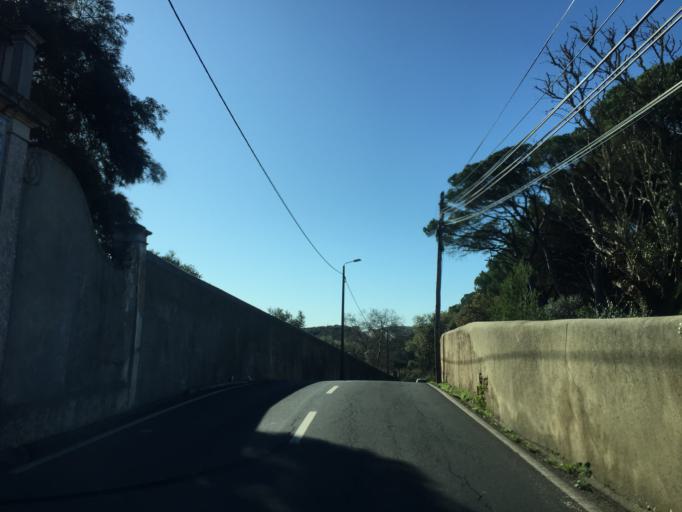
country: PT
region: Lisbon
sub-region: Sintra
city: Belas
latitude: 38.7820
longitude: -9.2649
